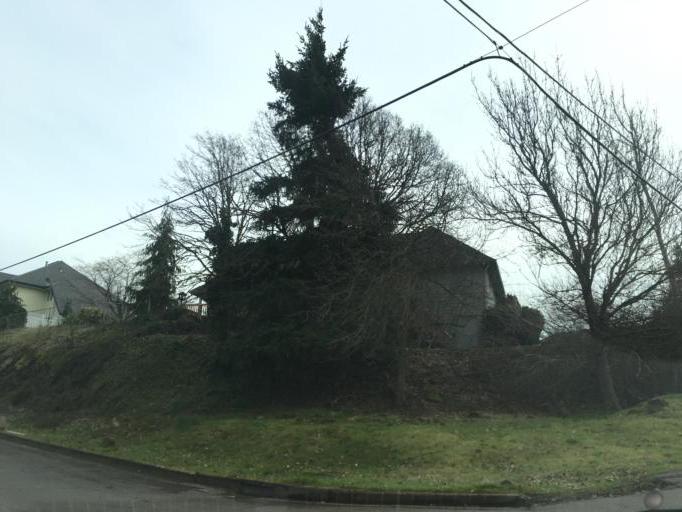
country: US
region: Oregon
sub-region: Hood River County
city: Hood River
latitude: 45.7075
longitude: -121.5390
